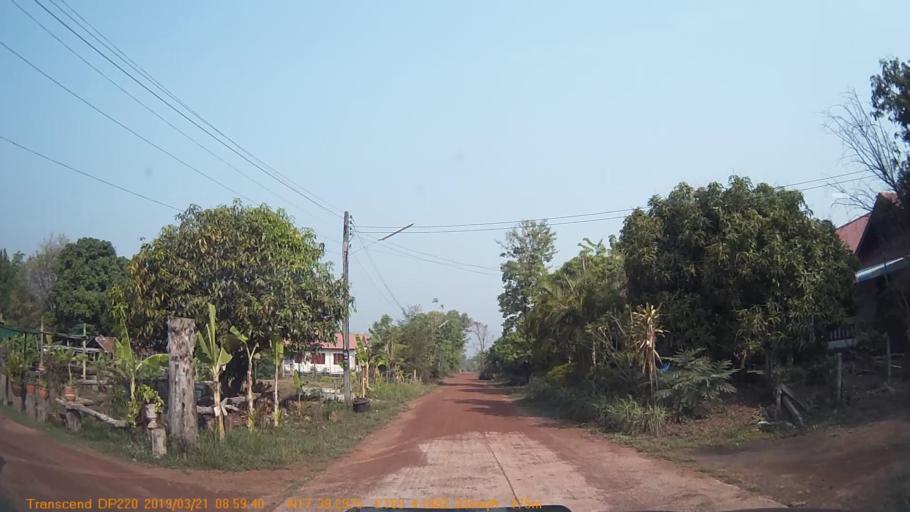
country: TH
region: Changwat Udon Thani
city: Phibun Rak
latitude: 17.6551
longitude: 103.0682
